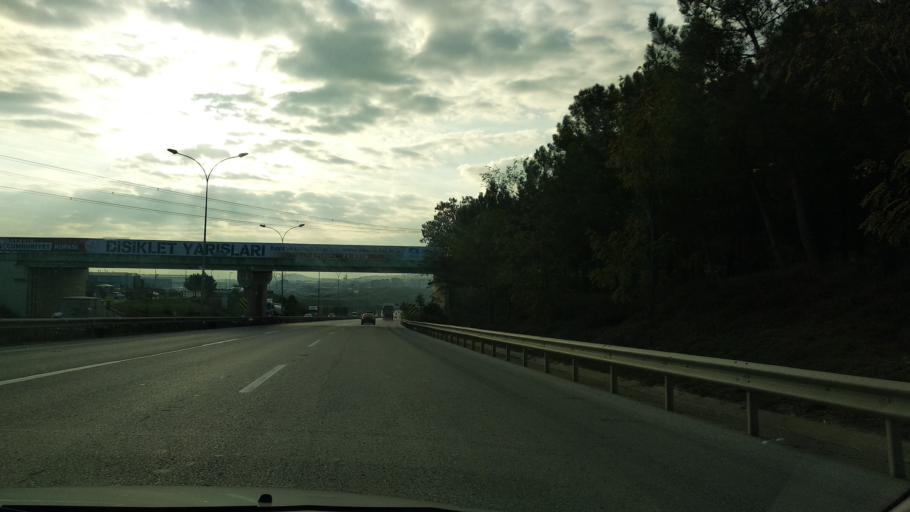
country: TR
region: Istanbul
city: Pendik
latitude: 40.9165
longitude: 29.3338
